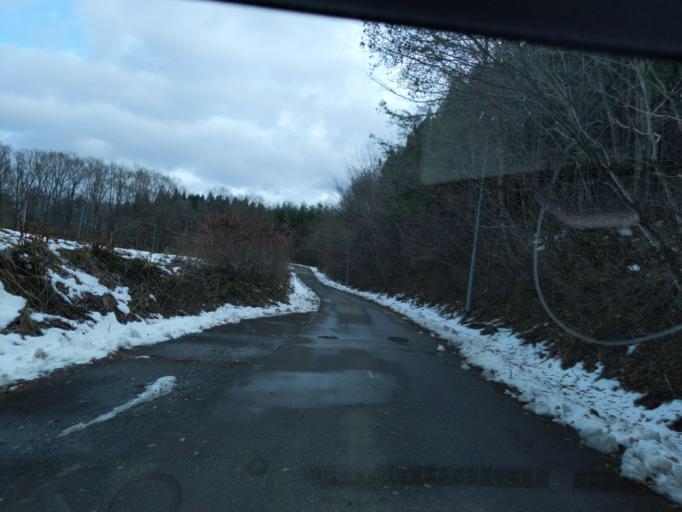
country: JP
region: Iwate
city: Ichinoseki
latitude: 38.9760
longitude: 141.0251
